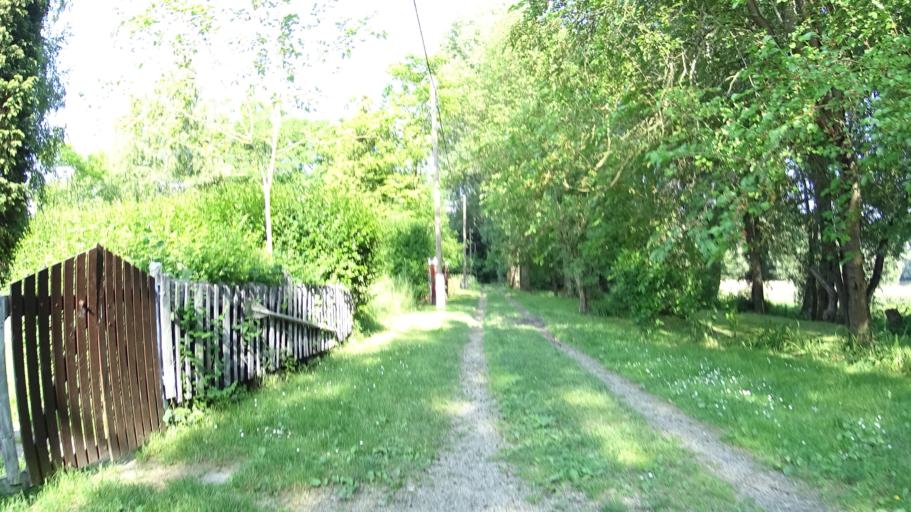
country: HU
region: Pest
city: Kismaros
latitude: 47.8079
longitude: 18.9984
